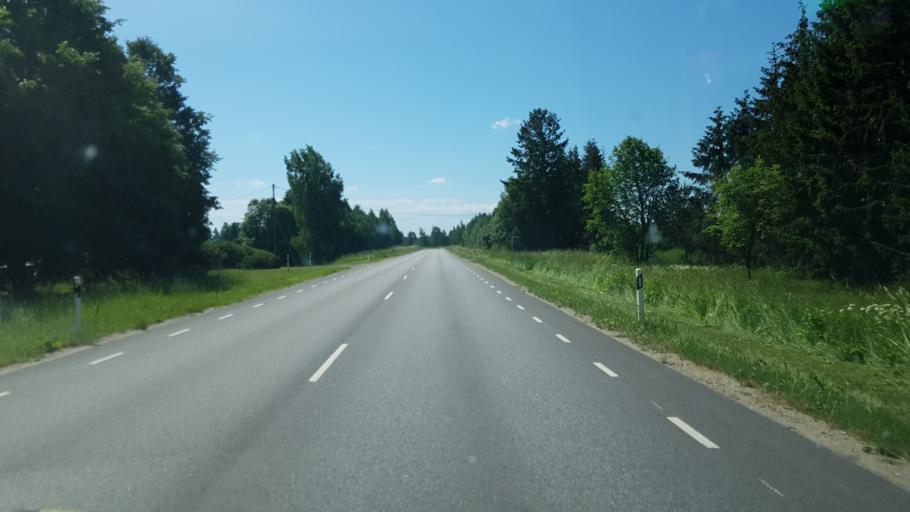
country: EE
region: Polvamaa
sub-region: Polva linn
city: Polva
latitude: 58.2561
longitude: 27.0025
